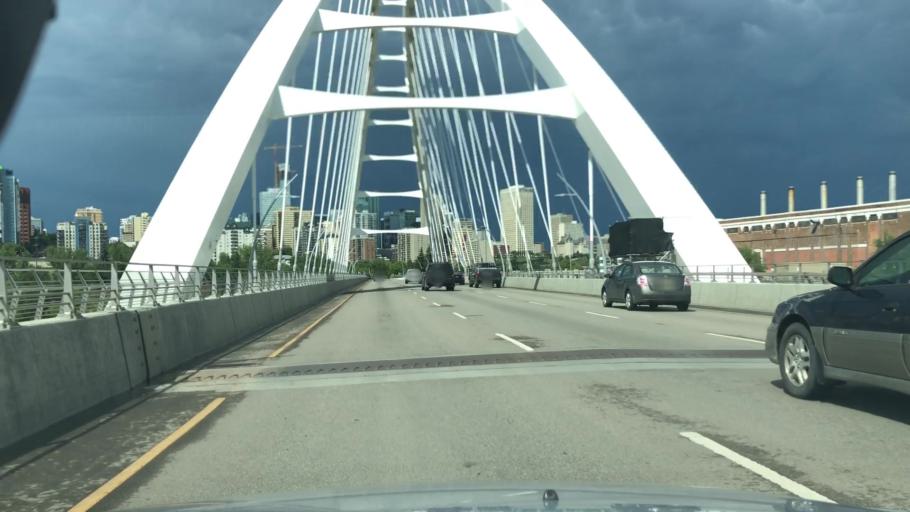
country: CA
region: Alberta
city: Edmonton
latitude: 53.5274
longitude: -113.5024
